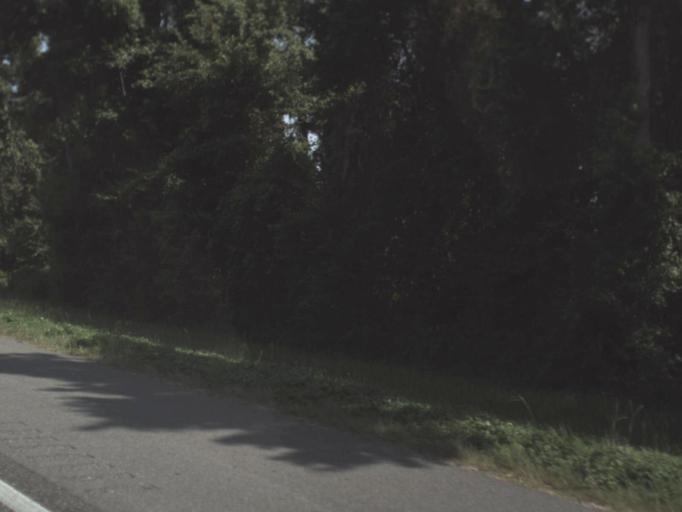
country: US
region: Florida
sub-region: Hamilton County
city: Jasper
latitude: 30.4383
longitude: -82.9161
